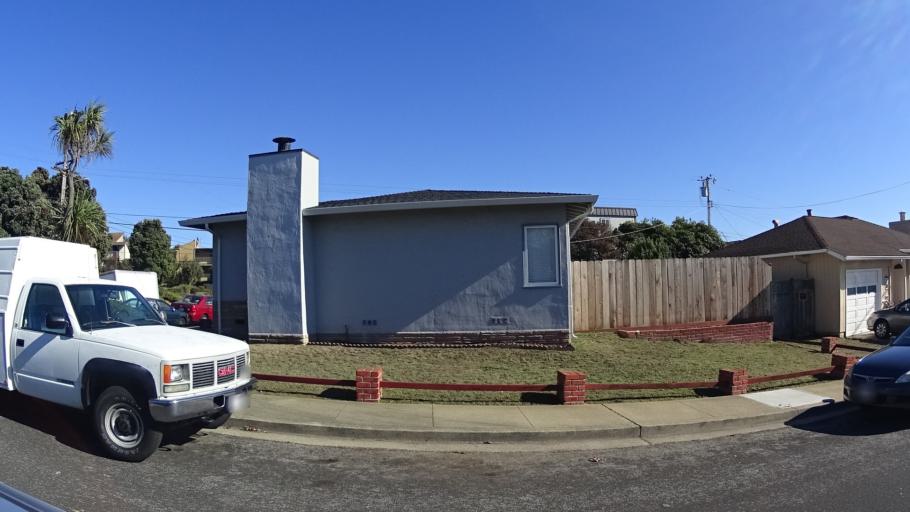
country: US
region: California
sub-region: San Mateo County
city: South San Francisco
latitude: 37.6616
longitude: -122.4338
